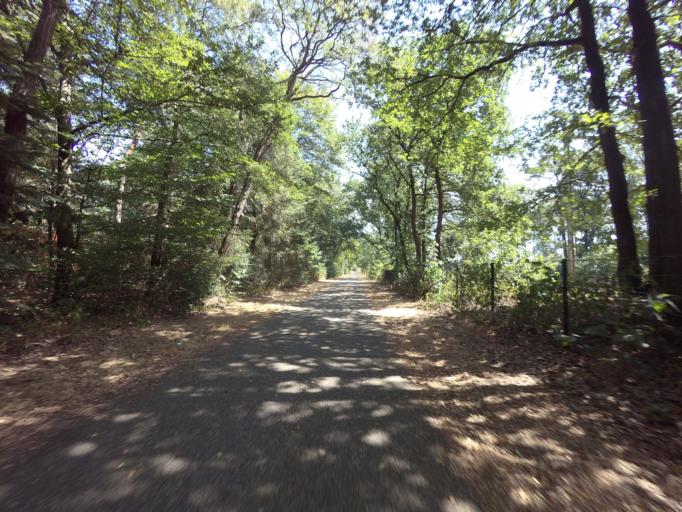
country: NL
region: Utrecht
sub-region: Gemeente Soest
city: Soest
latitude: 52.1451
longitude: 5.3041
